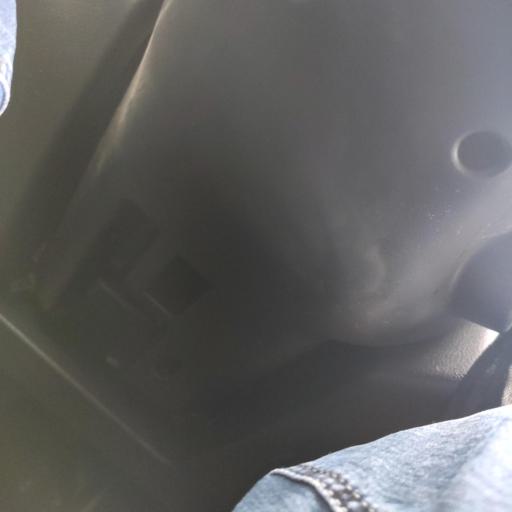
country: RU
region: Samara
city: Smyshlyayevka
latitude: 53.2109
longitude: 50.3278
